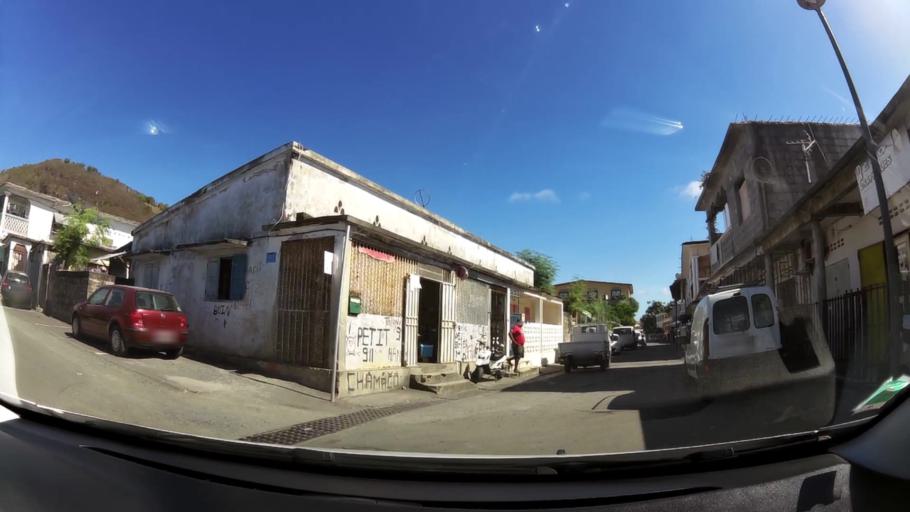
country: YT
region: Pamandzi
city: Pamandzi
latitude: -12.7870
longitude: 45.2738
